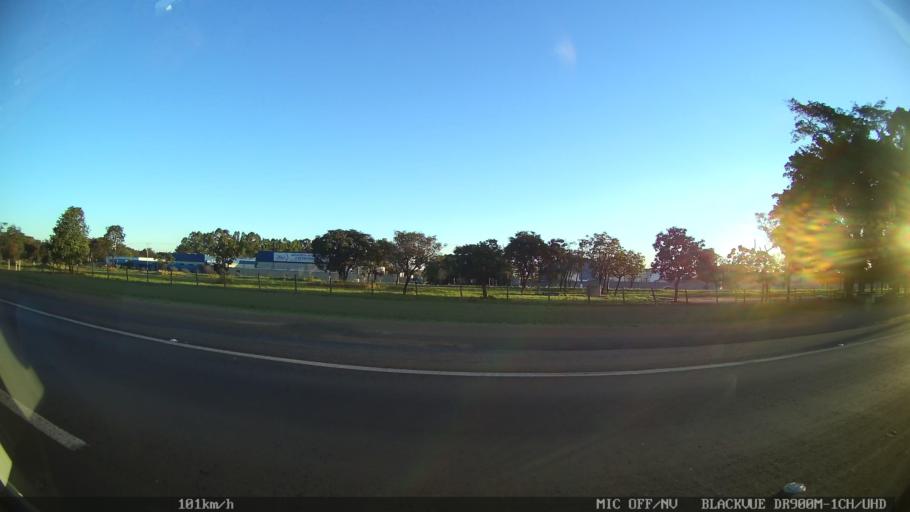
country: BR
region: Sao Paulo
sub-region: Ibate
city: Ibate
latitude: -21.9369
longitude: -48.0121
